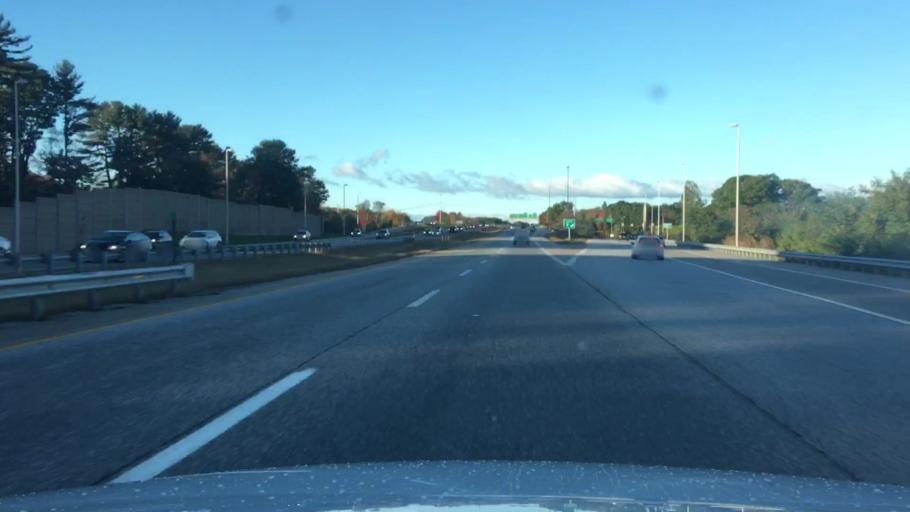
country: US
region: Maine
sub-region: Cumberland County
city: South Portland Gardens
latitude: 43.6332
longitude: -70.3073
